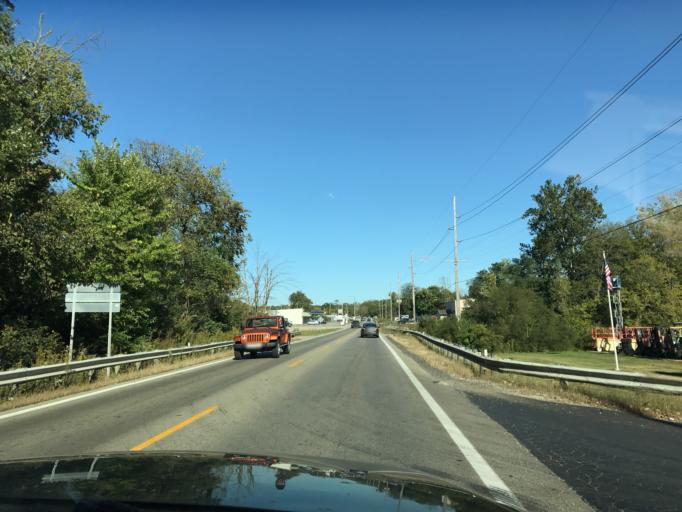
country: US
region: Ohio
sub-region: Franklin County
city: Grove City
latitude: 39.8070
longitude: -83.1705
